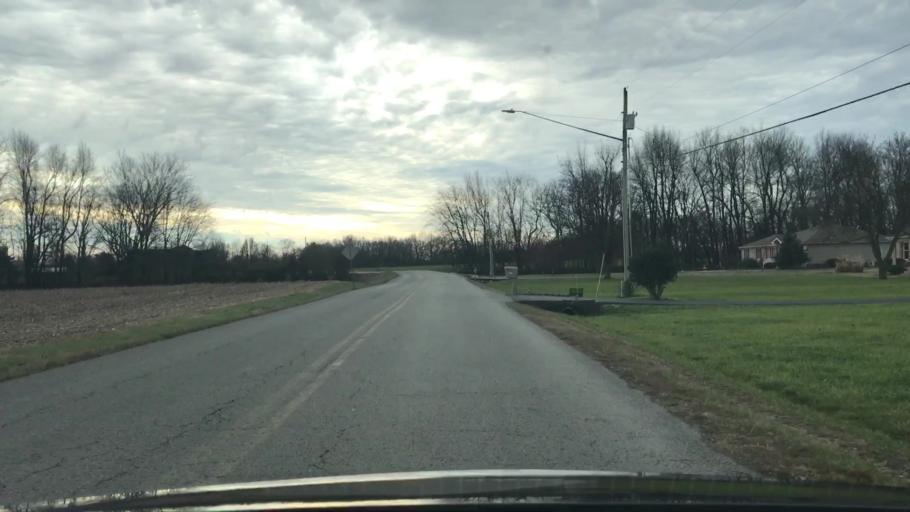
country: US
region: Kentucky
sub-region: Christian County
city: Hopkinsville
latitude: 36.8719
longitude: -87.5409
